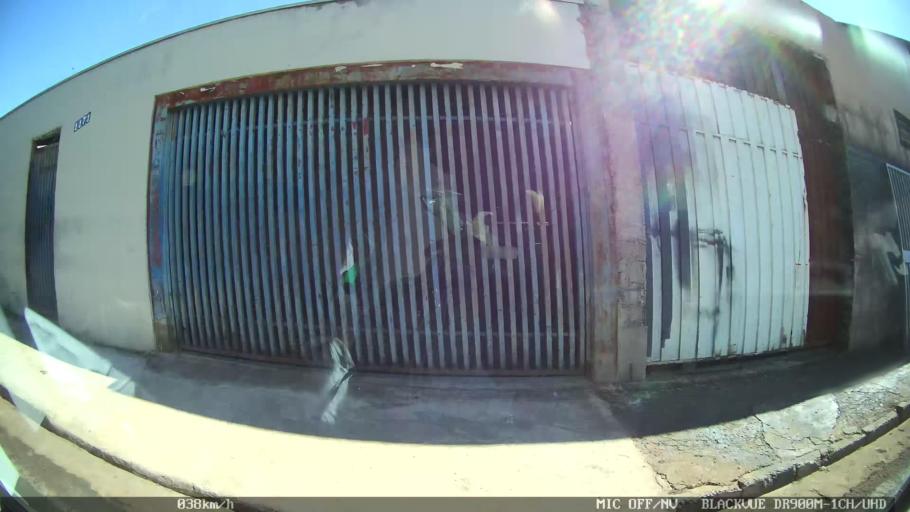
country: BR
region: Sao Paulo
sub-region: Sao Jose Do Rio Preto
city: Sao Jose do Rio Preto
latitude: -20.7711
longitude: -49.3991
